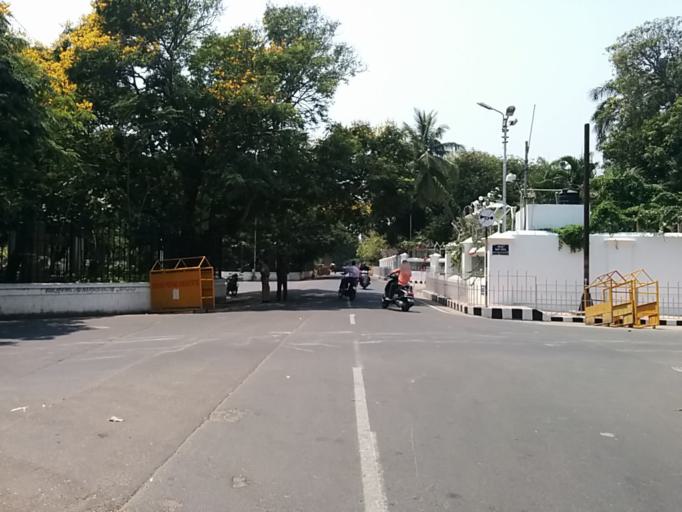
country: IN
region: Pondicherry
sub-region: Puducherry
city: Puducherry
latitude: 11.9341
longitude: 79.8349
